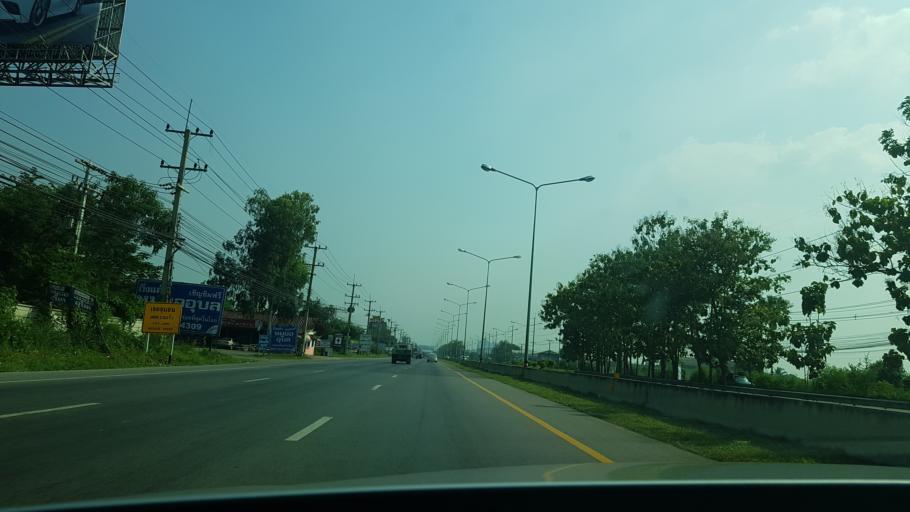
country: TH
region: Phetchaburi
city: Khao Yoi
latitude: 13.2714
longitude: 99.8203
